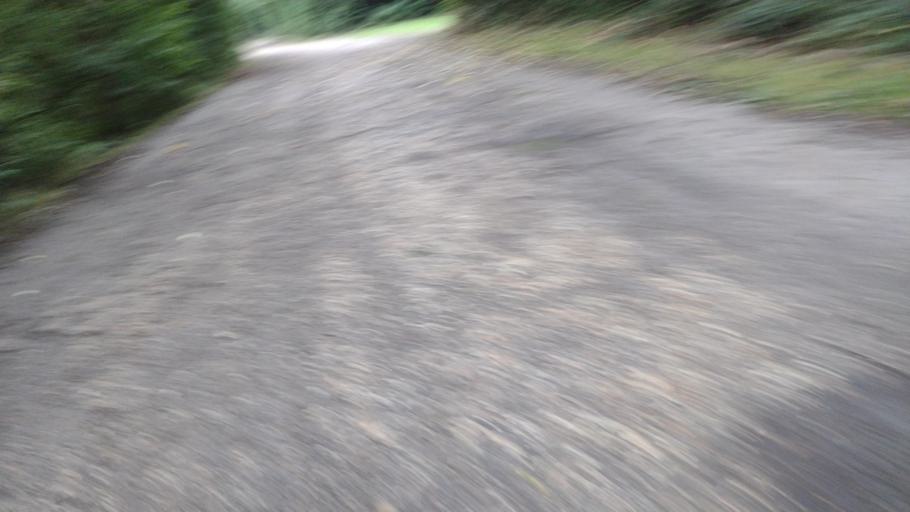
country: GB
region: England
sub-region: Wokingham
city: Woodley
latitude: 51.4409
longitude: -0.8841
